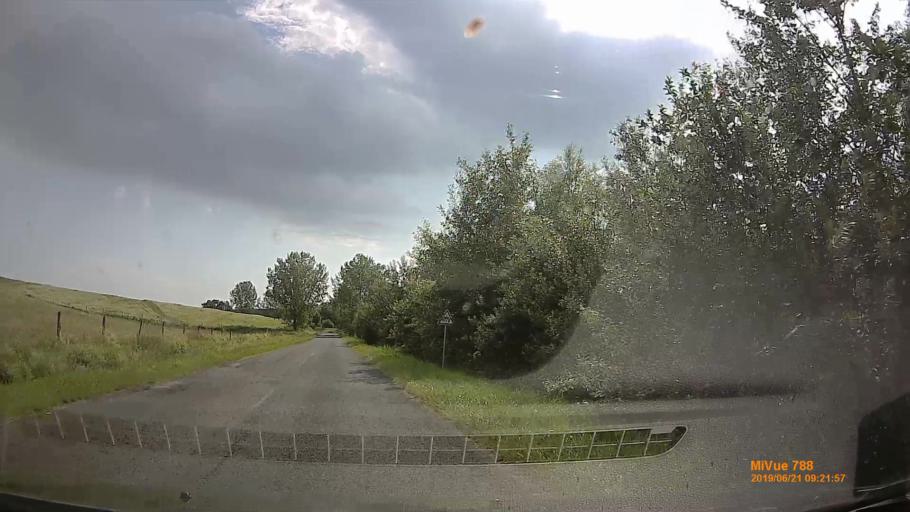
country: HU
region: Somogy
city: Taszar
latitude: 46.2440
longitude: 17.8870
